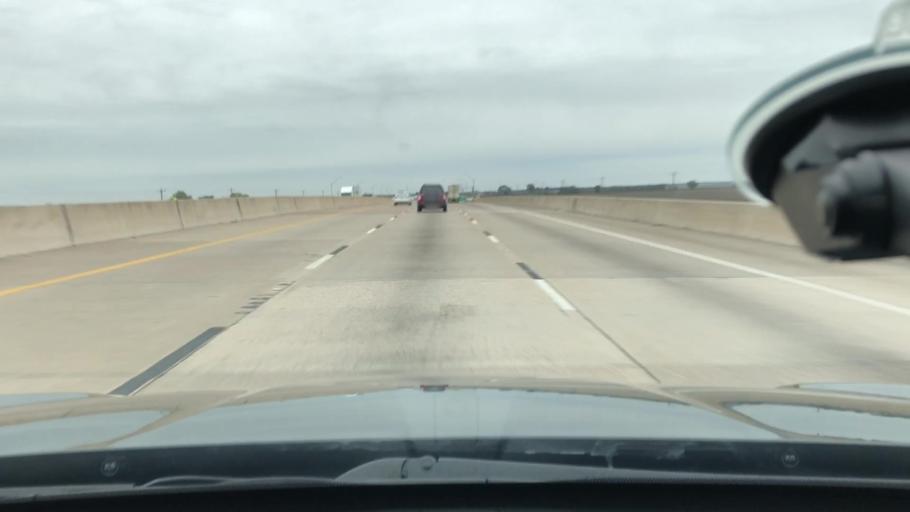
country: US
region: Texas
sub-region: Hill County
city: Hillsboro
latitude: 31.9384
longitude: -97.1072
